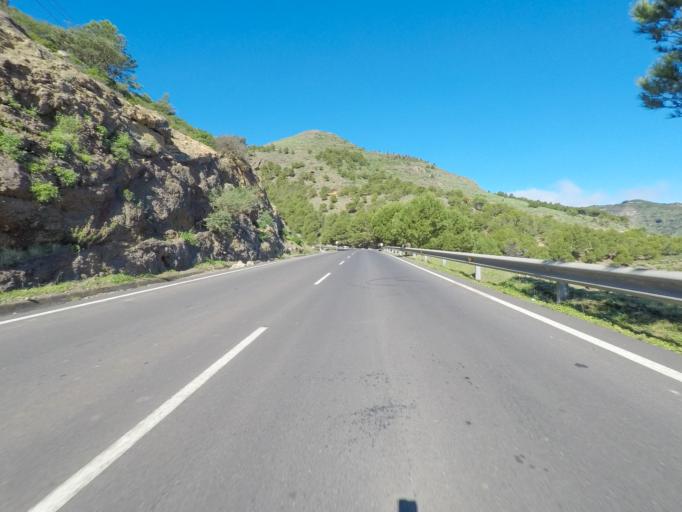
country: ES
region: Canary Islands
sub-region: Provincia de Santa Cruz de Tenerife
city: Alajero
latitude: 28.0833
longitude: -17.1994
